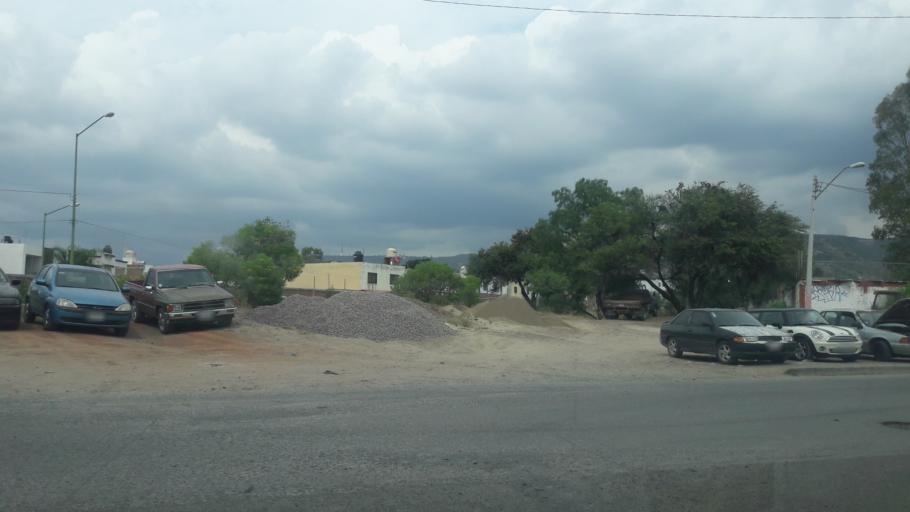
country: MX
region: Guanajuato
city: Leon
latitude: 21.1818
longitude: -101.6687
